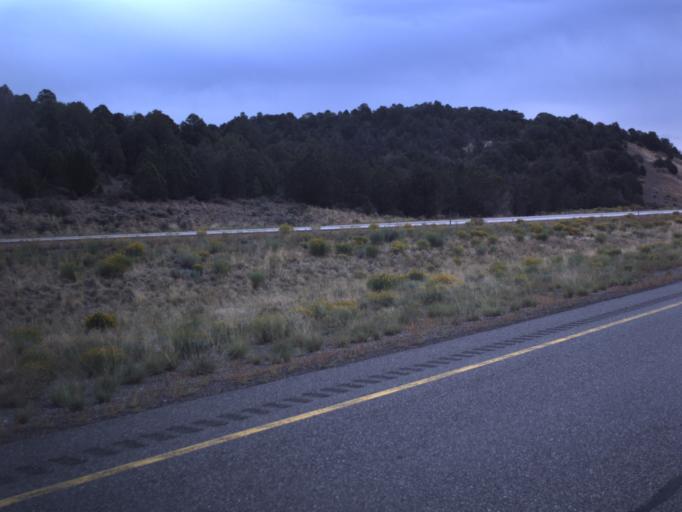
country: US
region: Utah
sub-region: Beaver County
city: Beaver
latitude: 38.5794
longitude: -112.4804
